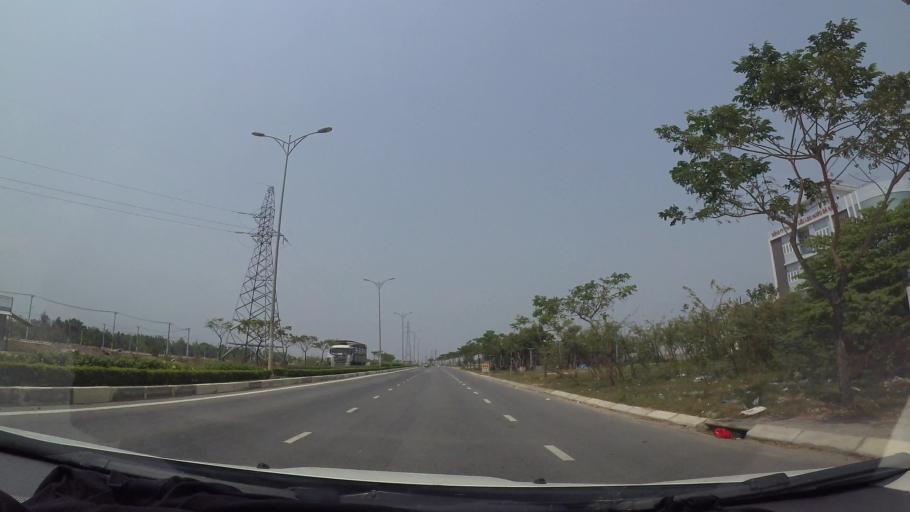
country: VN
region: Da Nang
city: Ngu Hanh Son
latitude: 15.9969
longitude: 108.2345
